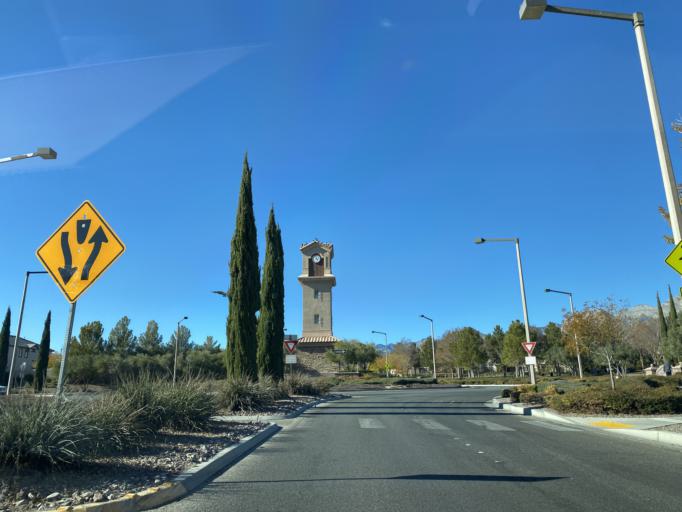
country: US
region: Nevada
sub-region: Clark County
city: Summerlin South
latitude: 36.1617
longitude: -115.3441
